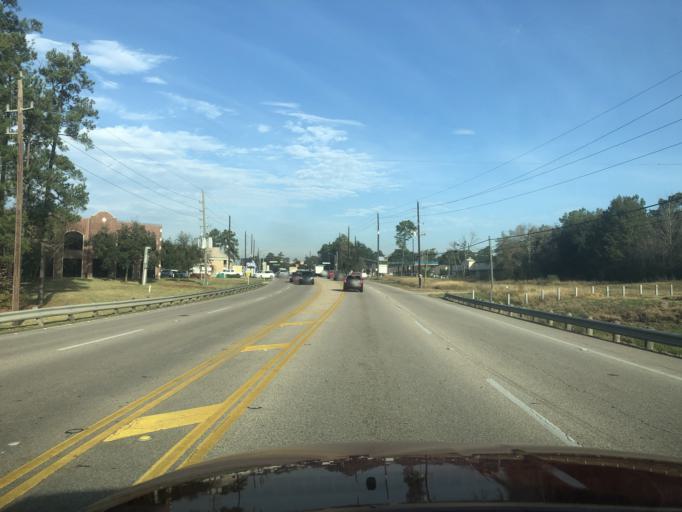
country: US
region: Texas
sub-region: Harris County
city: Spring
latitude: 30.0257
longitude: -95.4772
